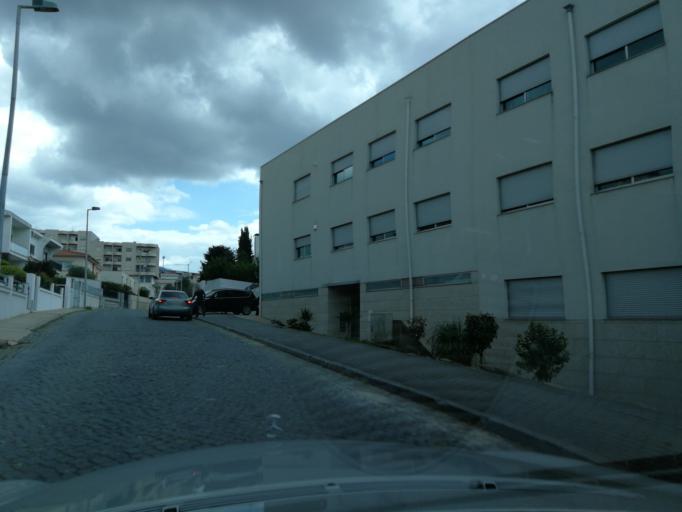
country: PT
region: Braga
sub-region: Braga
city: Braga
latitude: 41.5345
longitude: -8.4190
